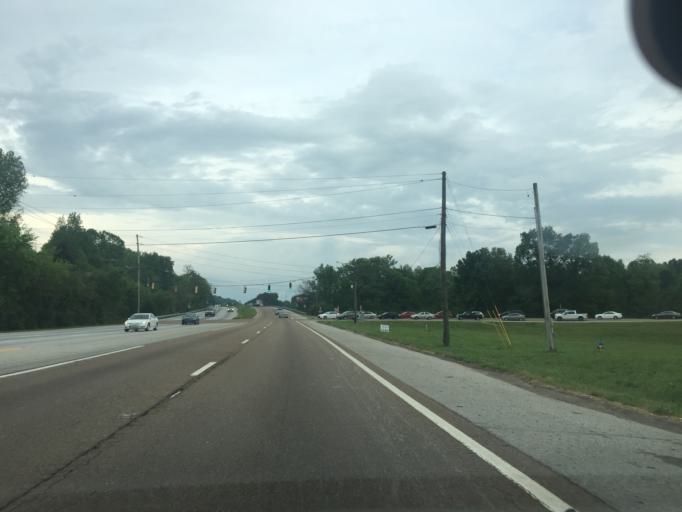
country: US
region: Tennessee
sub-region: Hamilton County
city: East Chattanooga
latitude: 35.1209
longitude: -85.2378
